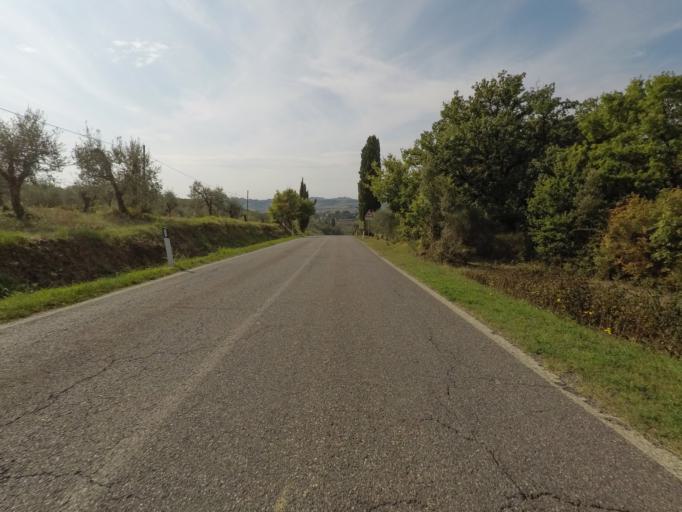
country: IT
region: Tuscany
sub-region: Provincia di Siena
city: Belverde
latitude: 43.3795
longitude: 11.3401
